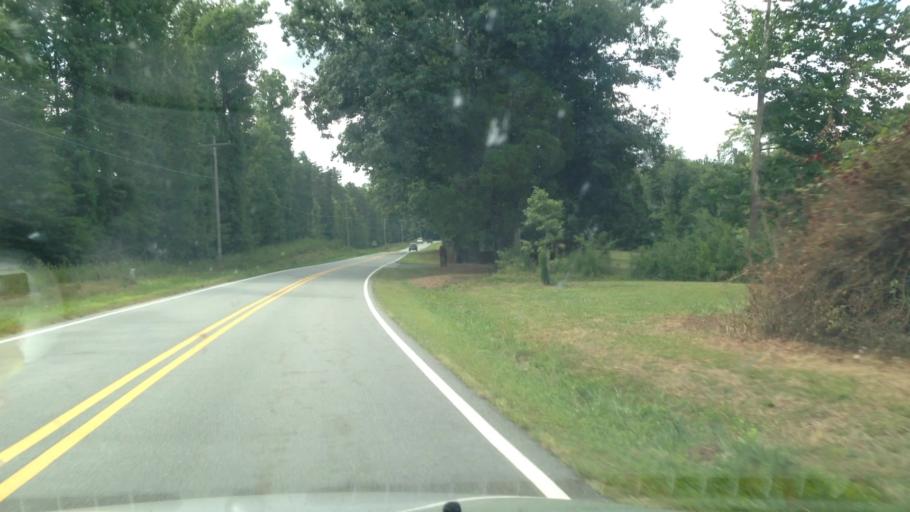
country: US
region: North Carolina
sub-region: Rockingham County
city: Mayodan
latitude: 36.3906
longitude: -80.0067
